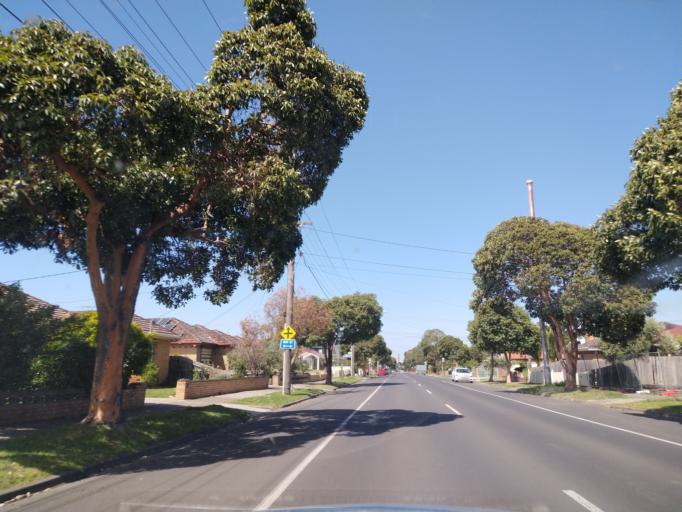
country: AU
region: Victoria
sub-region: Hobsons Bay
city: Altona North
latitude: -37.8332
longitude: 144.8562
